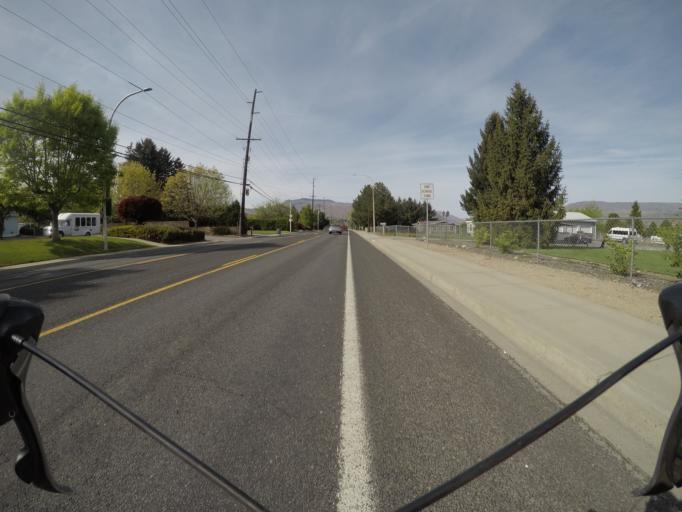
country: US
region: Washington
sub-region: Chelan County
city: West Wenatchee
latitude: 47.4338
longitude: -120.3463
